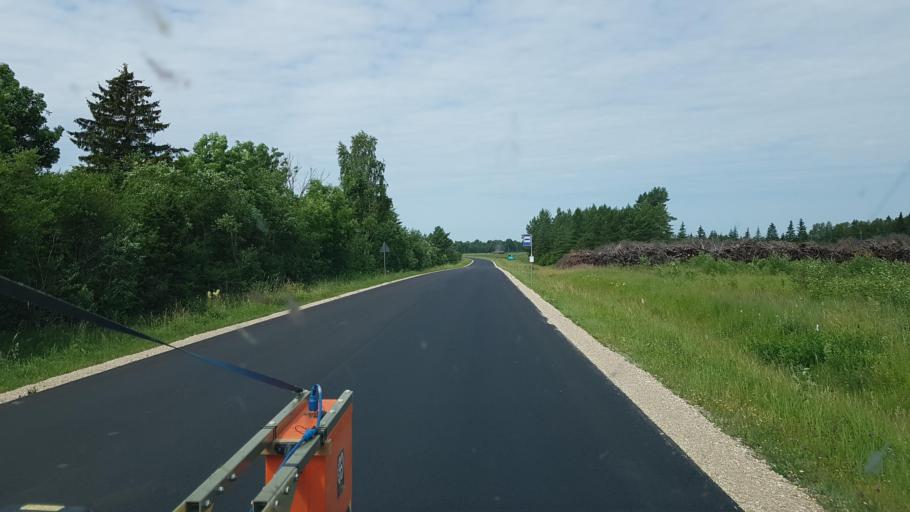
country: EE
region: Paernumaa
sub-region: Halinga vald
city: Parnu-Jaagupi
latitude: 58.6189
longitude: 24.2908
